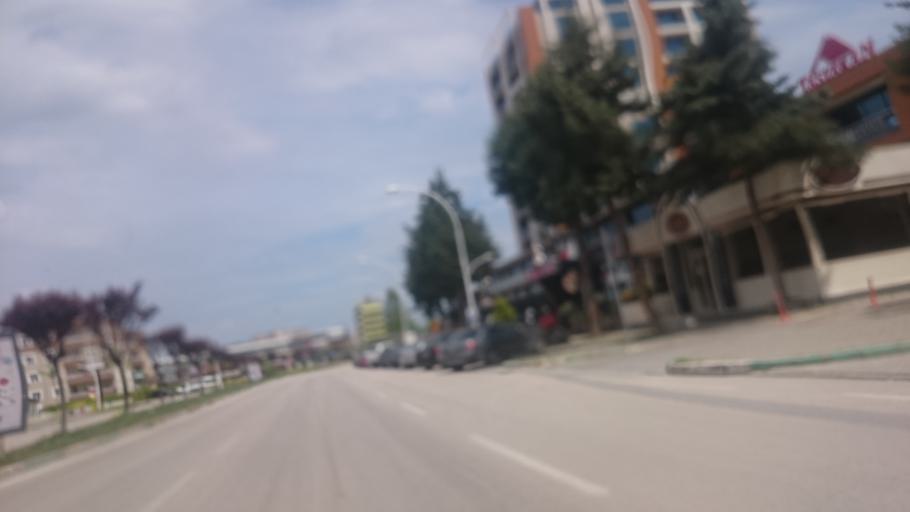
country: TR
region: Bursa
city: Cali
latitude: 40.2260
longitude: 28.9151
